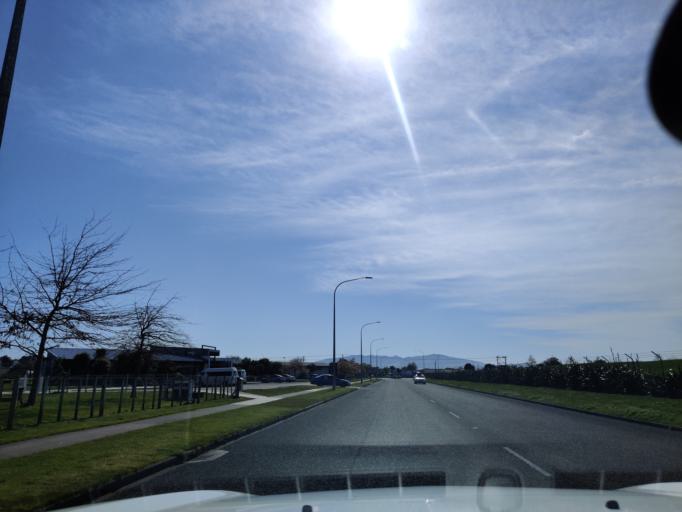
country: NZ
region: Manawatu-Wanganui
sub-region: Palmerston North City
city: Palmerston North
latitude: -40.3317
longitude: 175.6495
